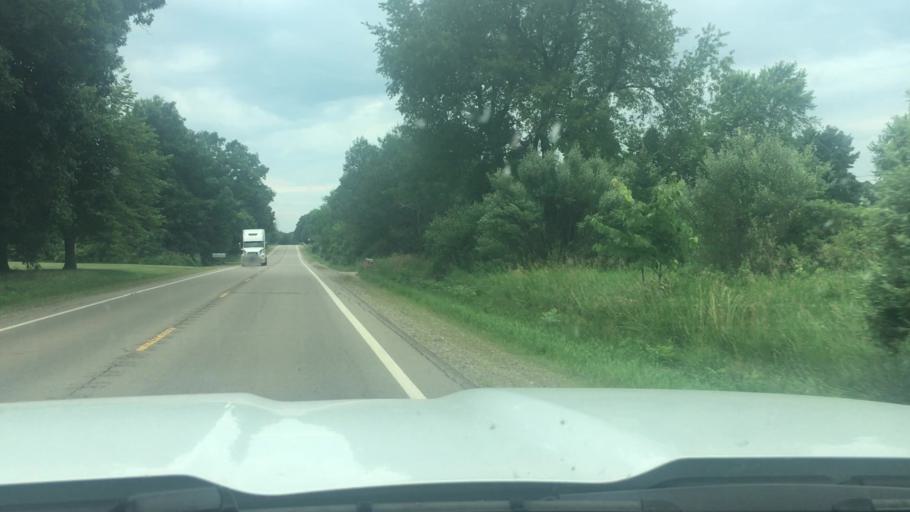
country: US
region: Michigan
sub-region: Ionia County
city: Portland
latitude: 43.0018
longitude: -84.8833
